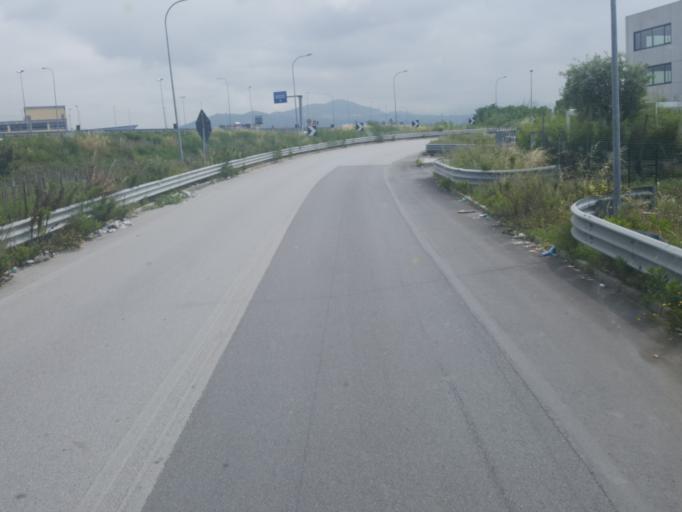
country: IT
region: Campania
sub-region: Provincia di Salerno
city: Fuorni
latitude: 40.6357
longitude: 14.8545
